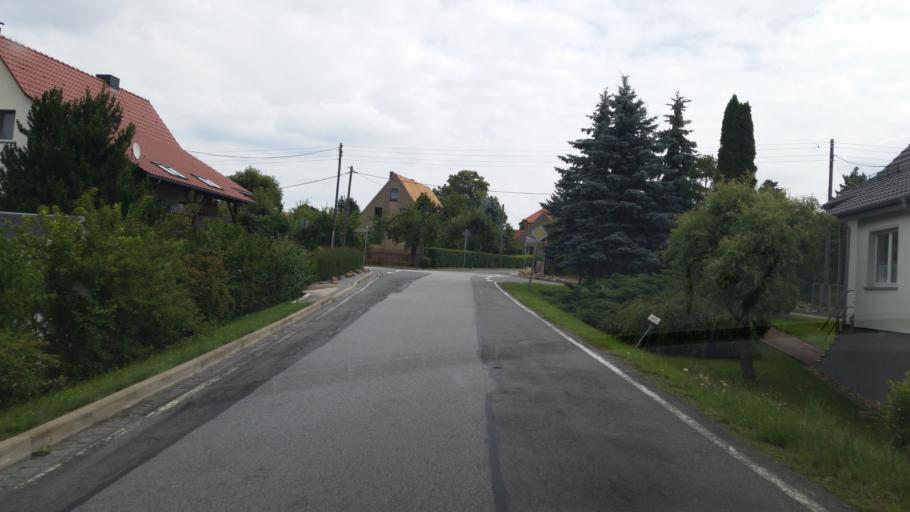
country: DE
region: Saxony
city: Radibor
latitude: 51.2131
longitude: 14.3901
